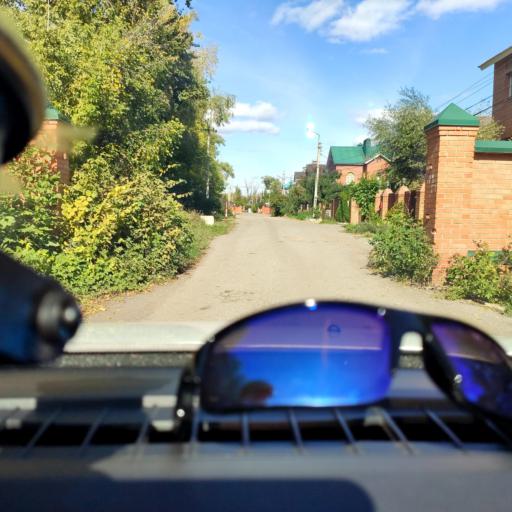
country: RU
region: Samara
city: Samara
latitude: 53.1545
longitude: 50.0821
